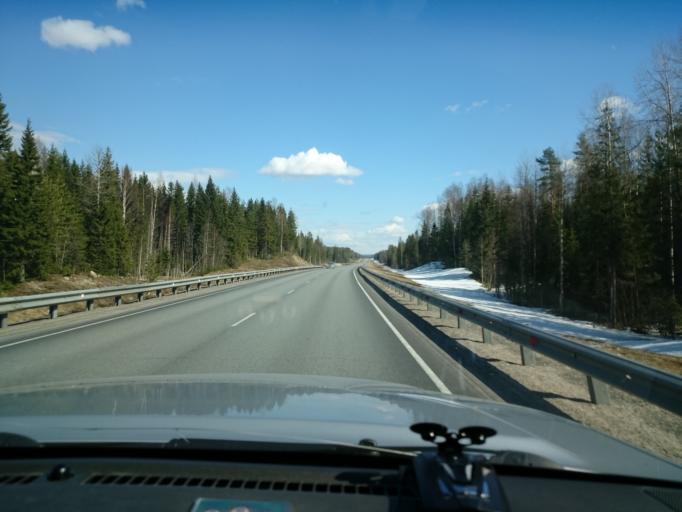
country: RU
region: Republic of Karelia
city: Pryazha
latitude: 61.5179
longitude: 33.4588
